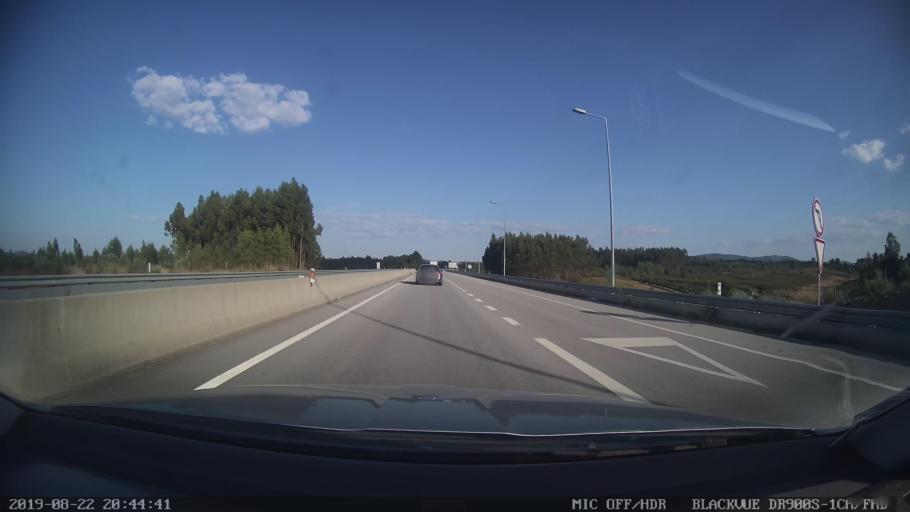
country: PT
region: Castelo Branco
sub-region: Proenca-A-Nova
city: Proenca-a-Nova
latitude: 39.7097
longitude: -7.8556
